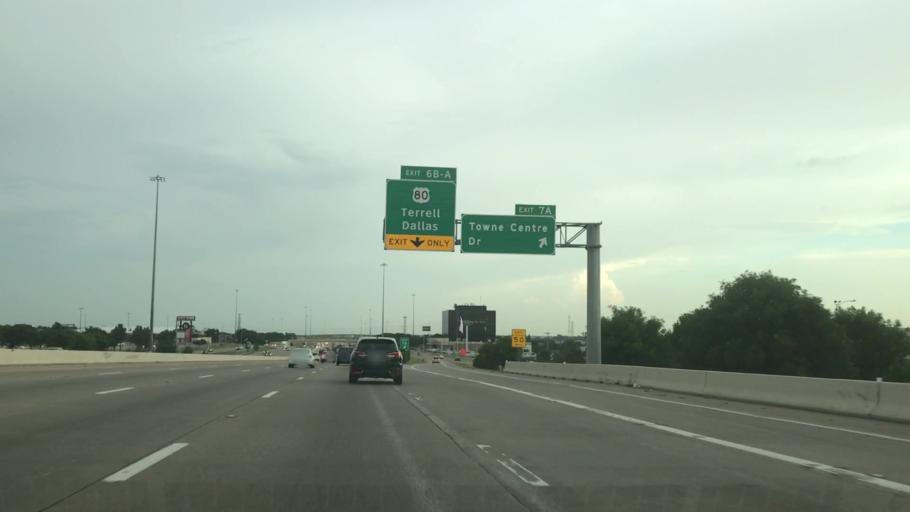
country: US
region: Texas
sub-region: Dallas County
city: Mesquite
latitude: 32.8095
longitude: -96.6278
